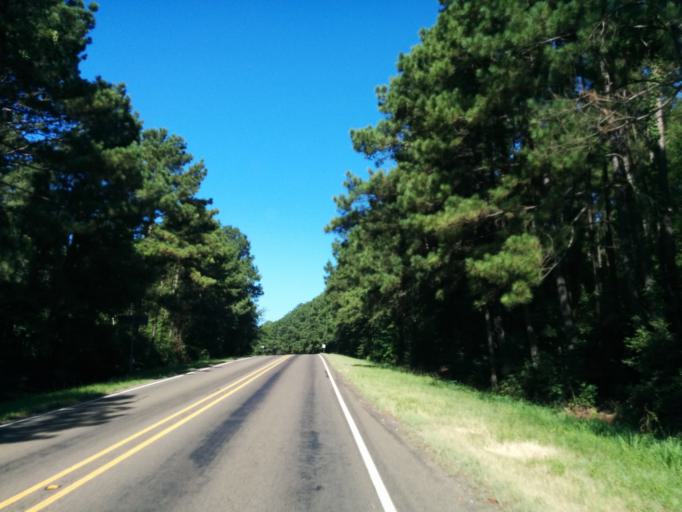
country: US
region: Texas
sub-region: Sabine County
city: Milam
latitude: 31.4352
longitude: -93.7846
